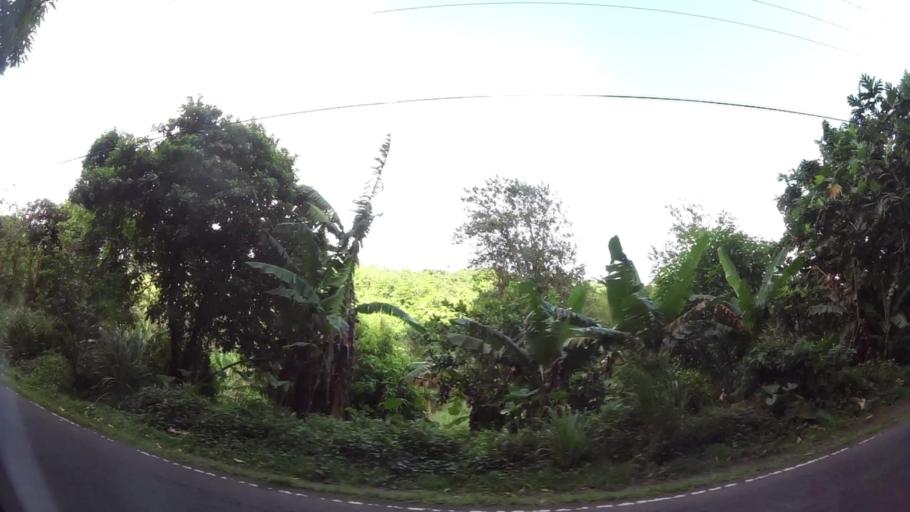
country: LC
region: Dennery Quarter
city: Dennery
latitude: 13.9338
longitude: -60.9339
